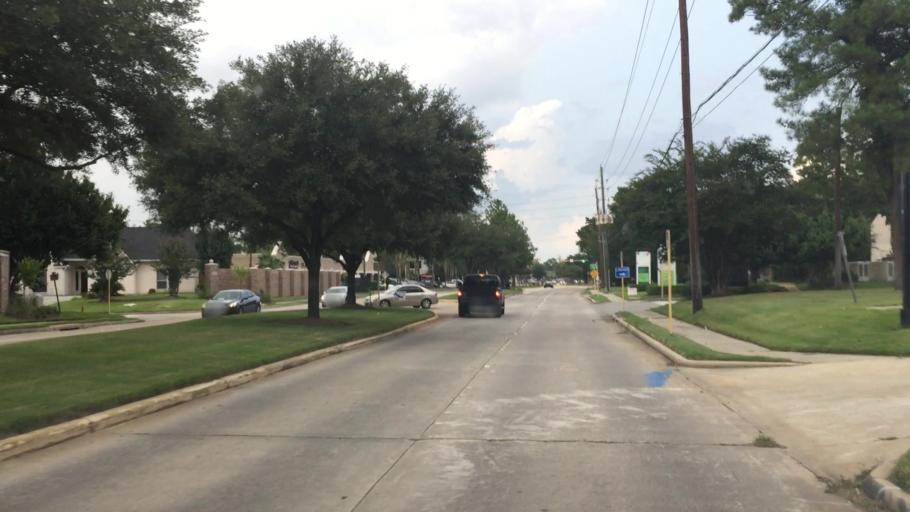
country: US
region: Texas
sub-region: Harris County
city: Hudson
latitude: 30.0128
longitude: -95.5110
